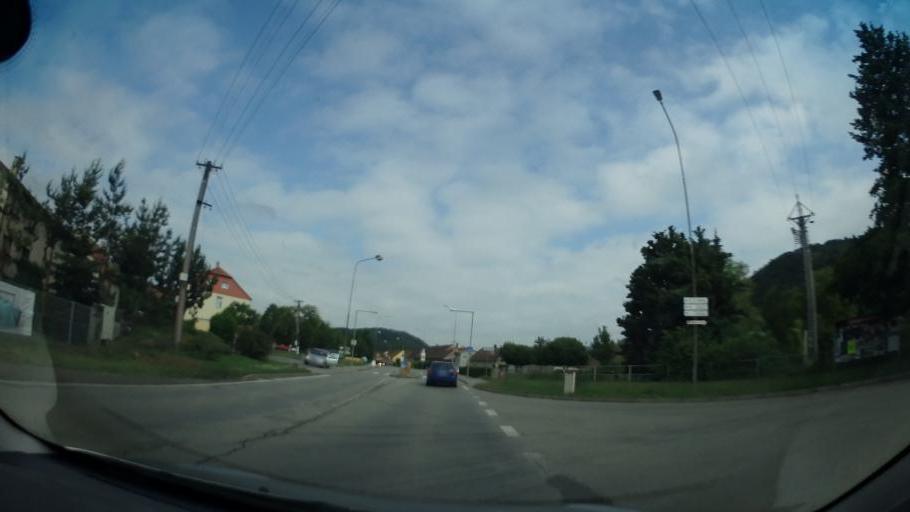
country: CZ
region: South Moravian
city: Predklasteri
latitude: 49.3515
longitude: 16.4081
